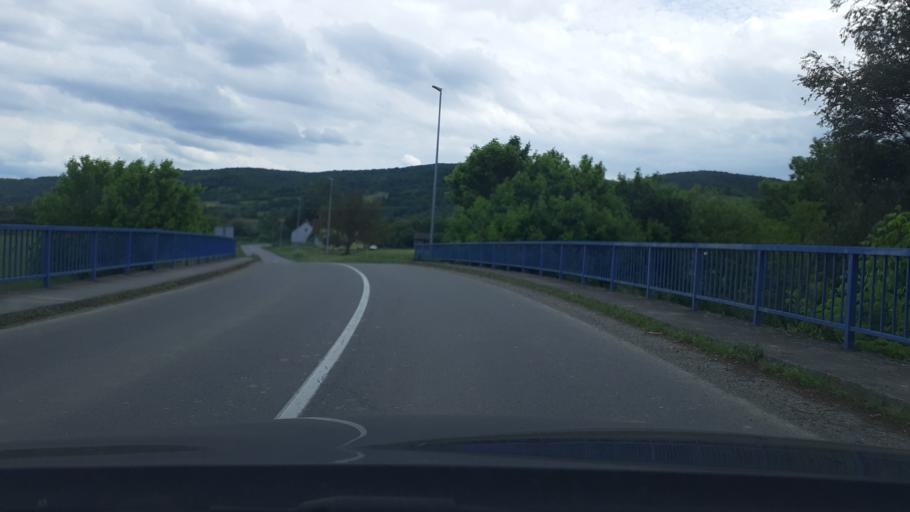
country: HR
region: Pozesko-Slavonska
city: Jaksic
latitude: 45.3312
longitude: 17.7554
